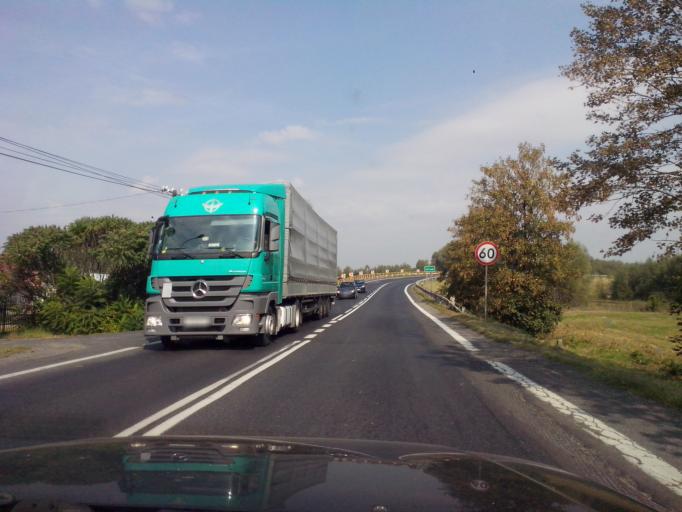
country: PL
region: Subcarpathian Voivodeship
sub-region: Powiat rzeszowski
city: Lutoryz
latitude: 49.9705
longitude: 21.9214
